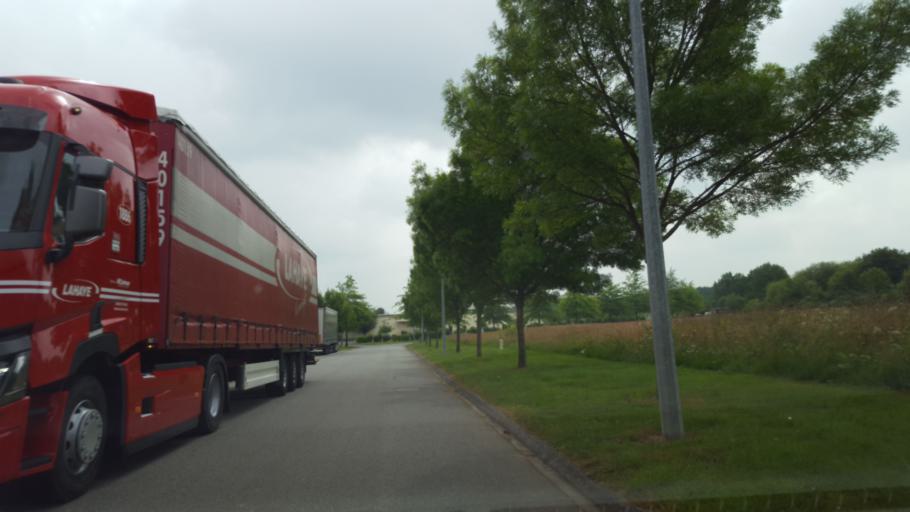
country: FR
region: Brittany
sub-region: Departement d'Ille-et-Vilaine
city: Grand-Fougeray
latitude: 47.7457
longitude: -1.7198
